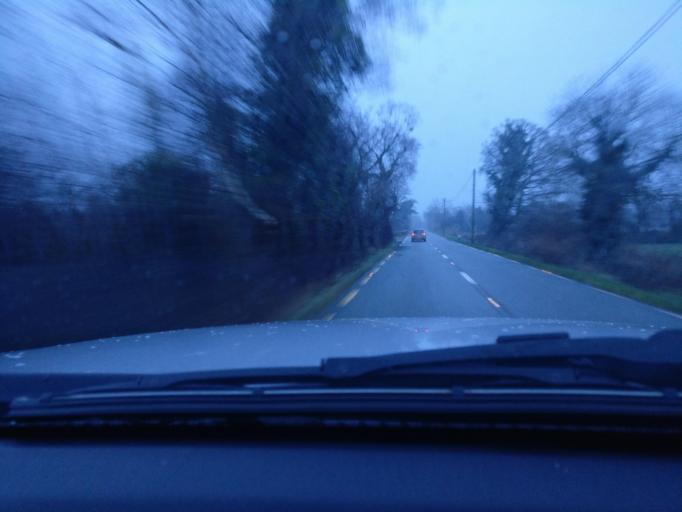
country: IE
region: Leinster
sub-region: An Mhi
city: Athboy
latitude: 53.6419
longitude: -6.8412
